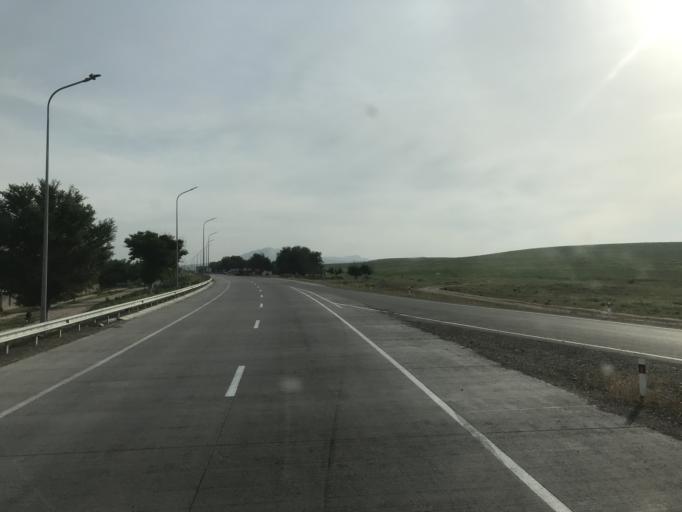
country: KZ
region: Ongtustik Qazaqstan
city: Qazyqurt
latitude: 41.9015
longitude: 69.4611
